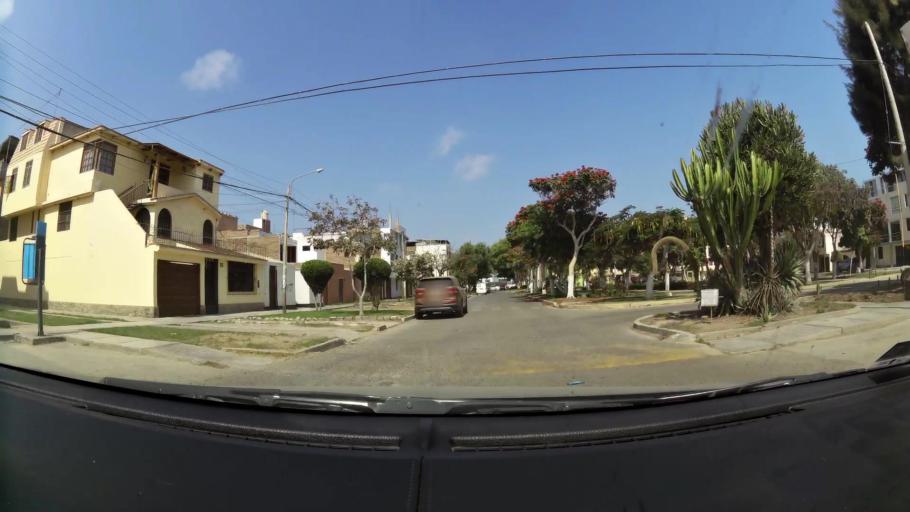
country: PE
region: La Libertad
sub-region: Provincia de Trujillo
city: Buenos Aires
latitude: -8.1266
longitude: -79.0434
